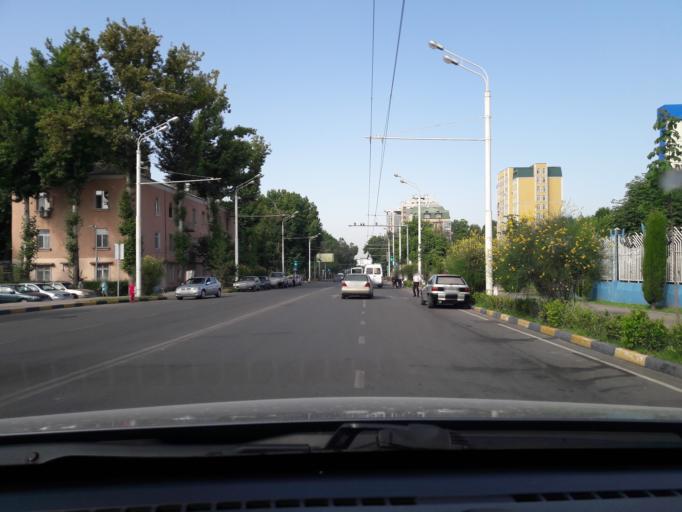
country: TJ
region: Dushanbe
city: Dushanbe
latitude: 38.5731
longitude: 68.8014
